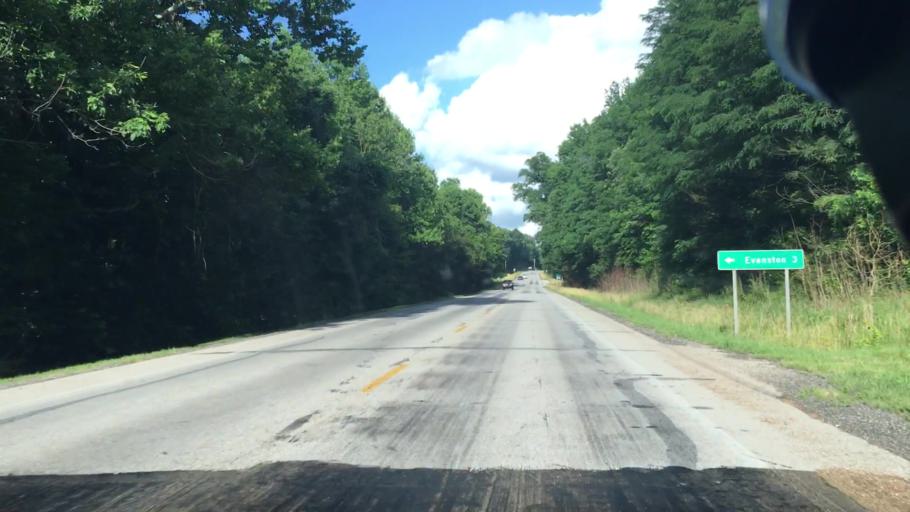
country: US
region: Indiana
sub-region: Perry County
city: Tell City
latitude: 38.0014
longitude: -86.8370
